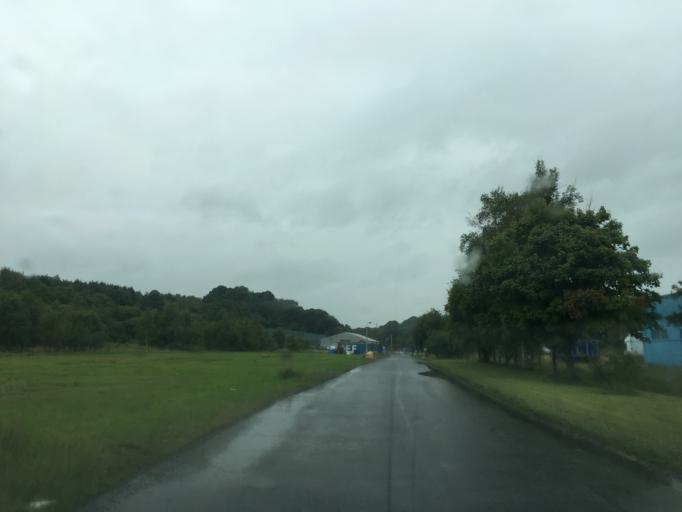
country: GB
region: Scotland
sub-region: Fife
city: Townhill
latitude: 56.1133
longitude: -3.4537
